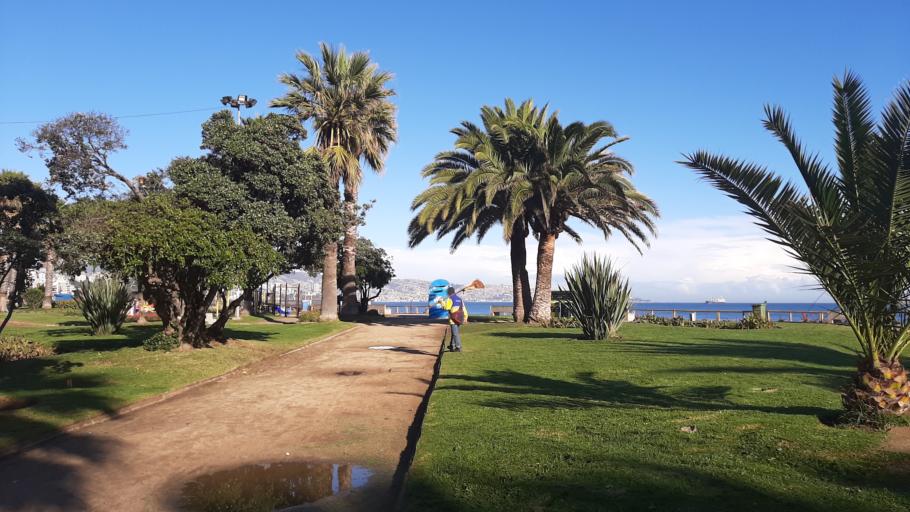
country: CL
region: Valparaiso
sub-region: Provincia de Valparaiso
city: Vina del Mar
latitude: -33.0091
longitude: -71.5517
